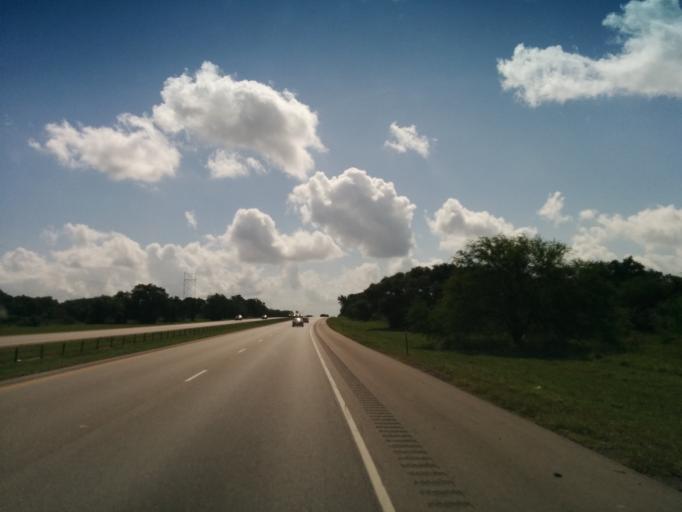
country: US
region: Texas
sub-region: Colorado County
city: Columbus
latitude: 29.6931
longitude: -96.6215
